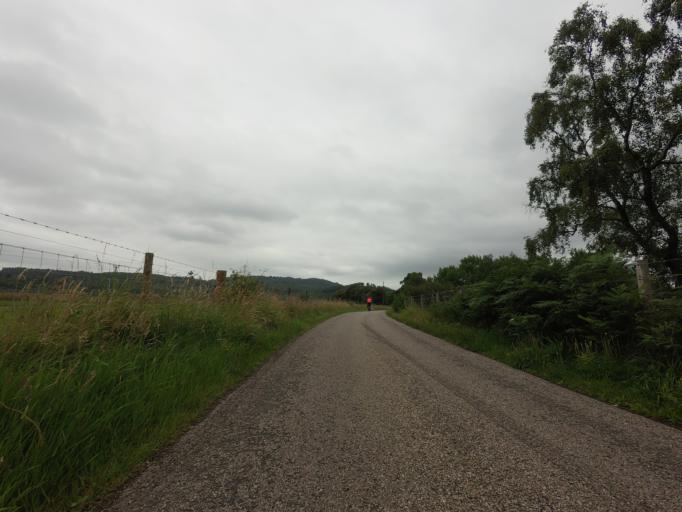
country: GB
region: Scotland
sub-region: Highland
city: Evanton
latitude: 57.9161
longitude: -4.4016
